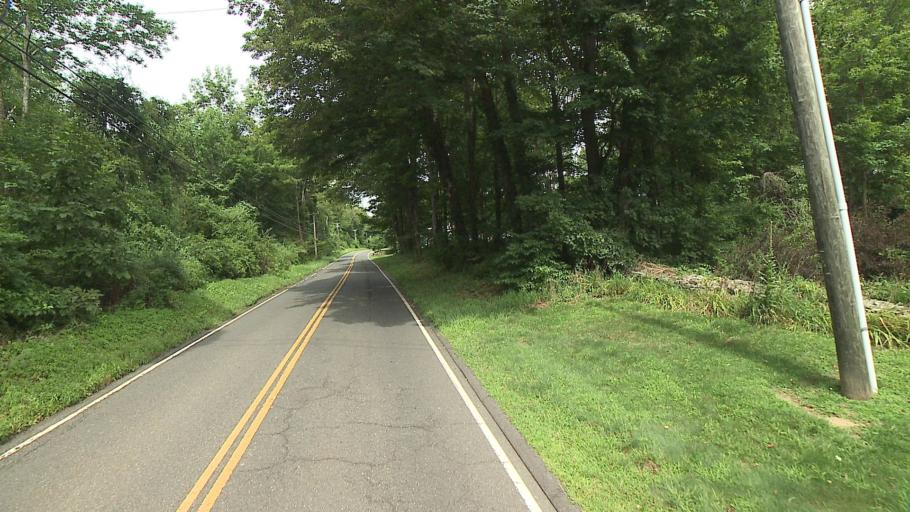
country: US
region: Connecticut
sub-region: Litchfield County
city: Woodbury
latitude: 41.5592
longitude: -73.2853
